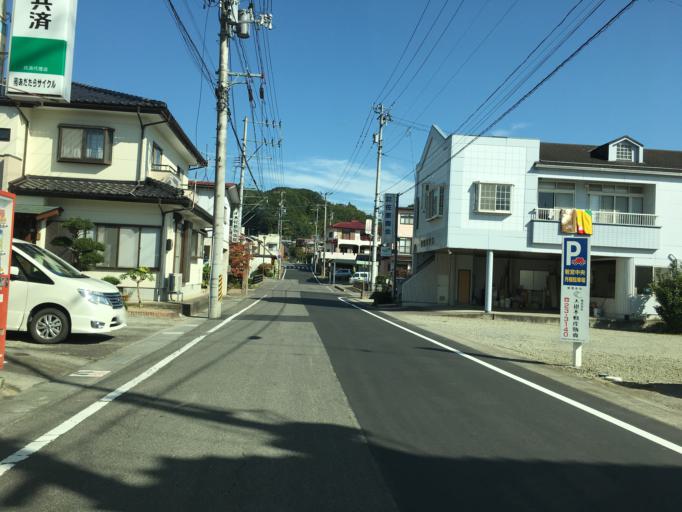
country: JP
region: Fukushima
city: Nihommatsu
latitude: 37.5902
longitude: 140.4273
